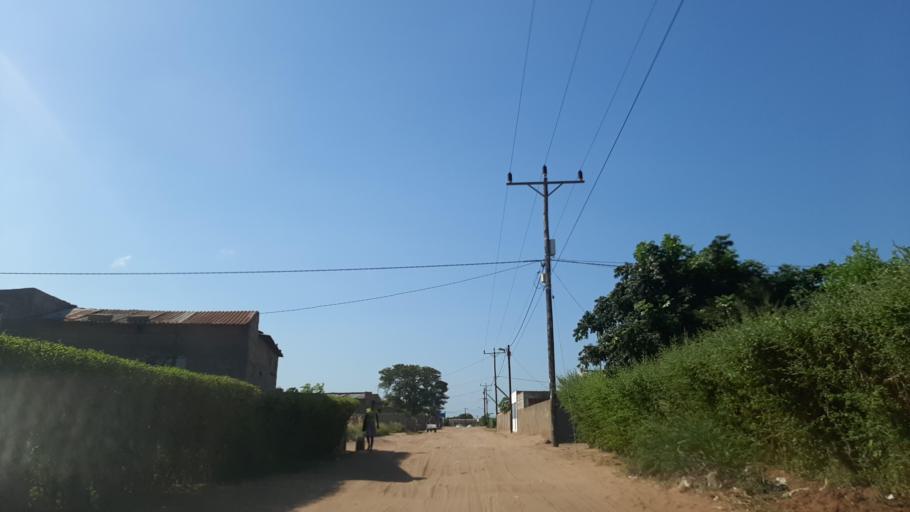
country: MZ
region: Maputo
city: Matola
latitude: -25.8020
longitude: 32.4909
